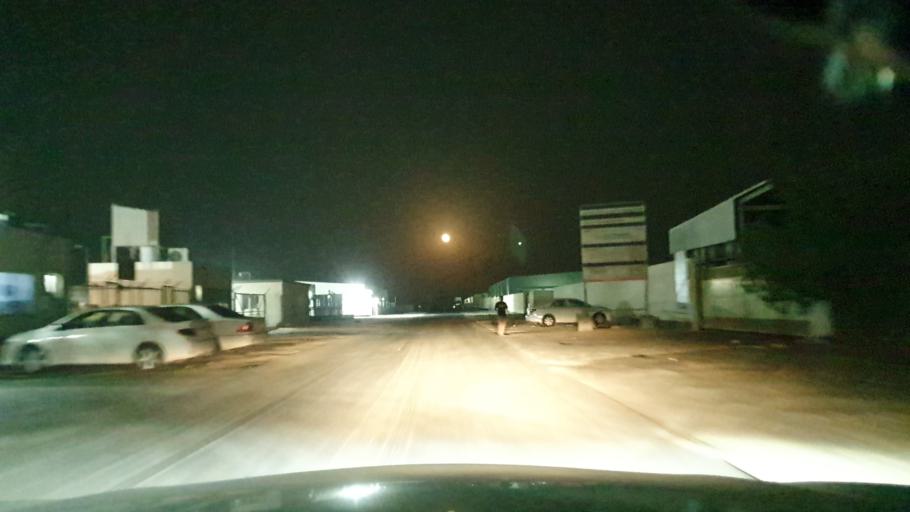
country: BH
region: Northern
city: Sitrah
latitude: 26.0973
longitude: 50.6217
